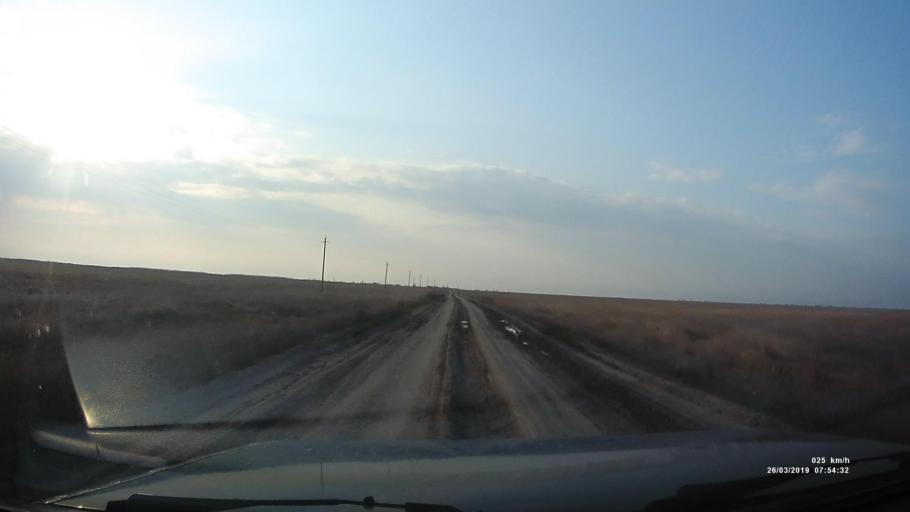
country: RU
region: Krasnodarskiy
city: Shabel'skoye
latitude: 47.1321
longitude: 38.5518
